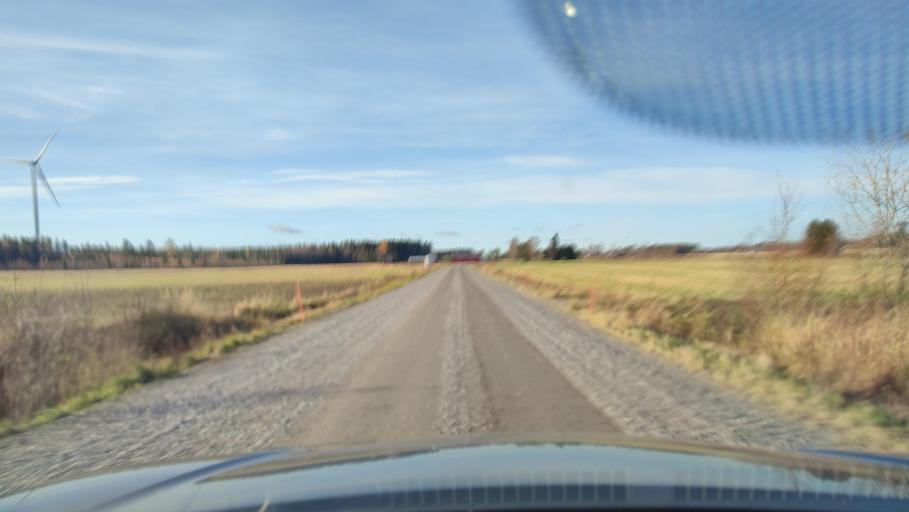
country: FI
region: Southern Ostrobothnia
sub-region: Suupohja
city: Teuva
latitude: 62.4583
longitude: 21.6719
